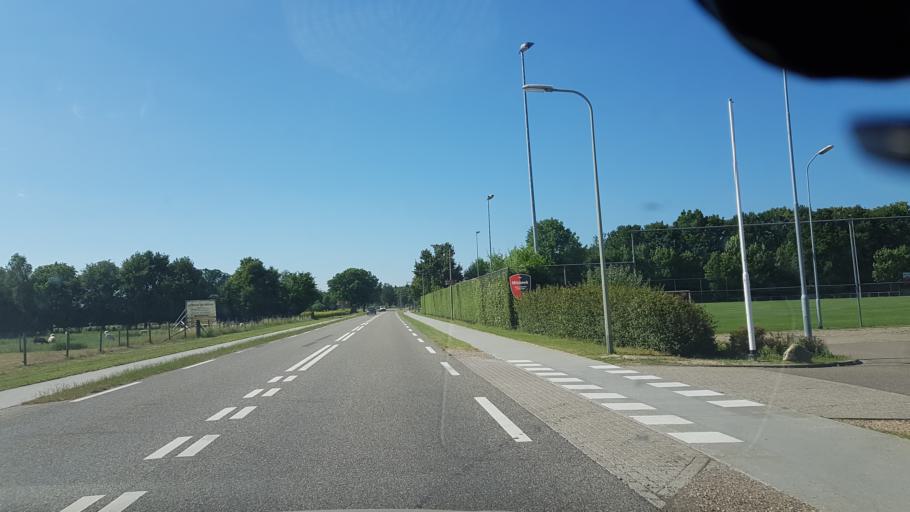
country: NL
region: Gelderland
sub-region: Gemeente Groesbeek
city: Bredeweg
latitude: 51.7343
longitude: 5.9556
